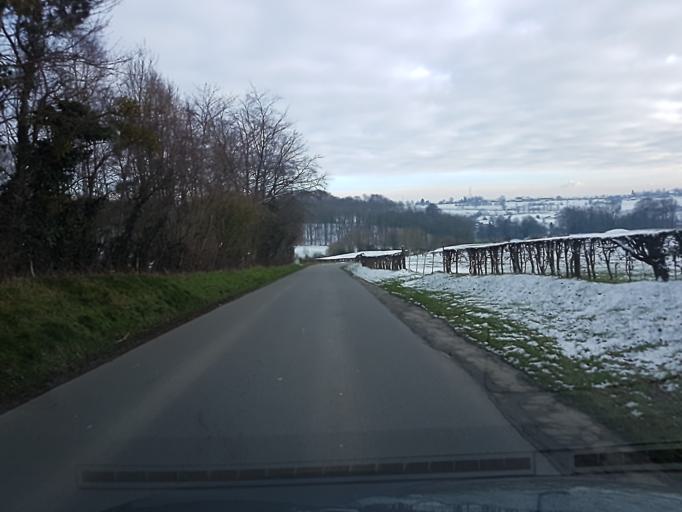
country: BE
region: Wallonia
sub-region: Province de Liege
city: Pepinster
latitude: 50.6005
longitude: 5.7879
